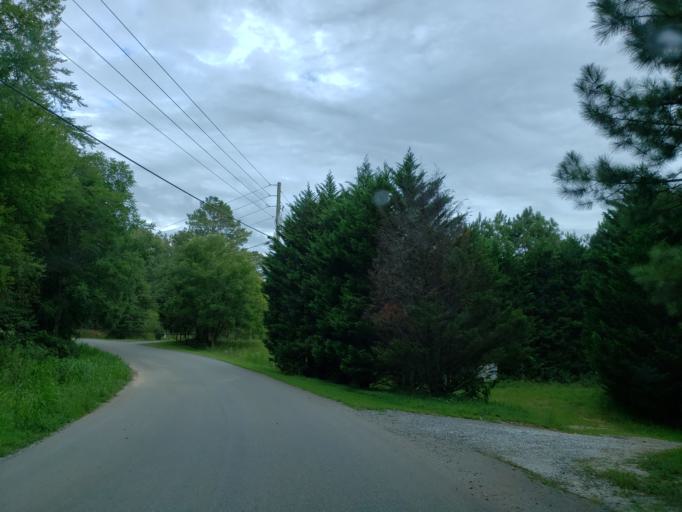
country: US
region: Georgia
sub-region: Pickens County
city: Jasper
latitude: 34.5272
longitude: -84.5139
